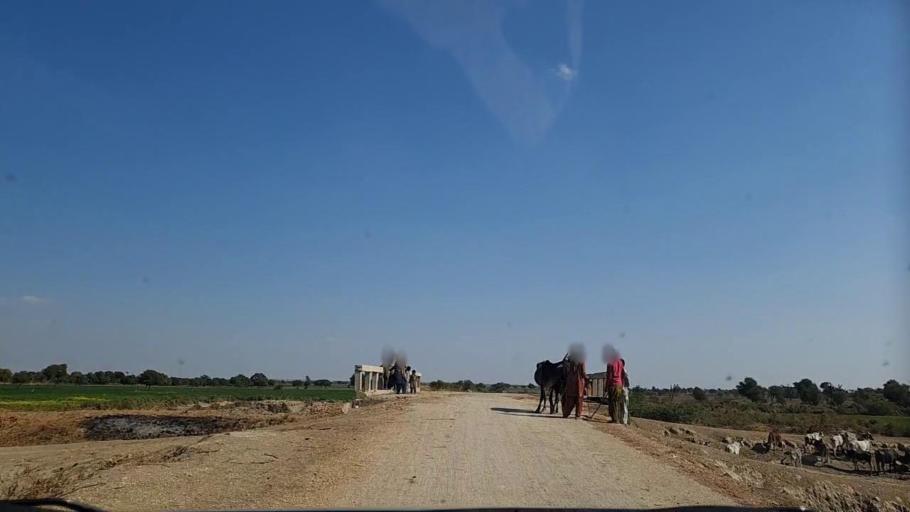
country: PK
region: Sindh
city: Pithoro
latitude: 25.6865
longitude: 69.4478
